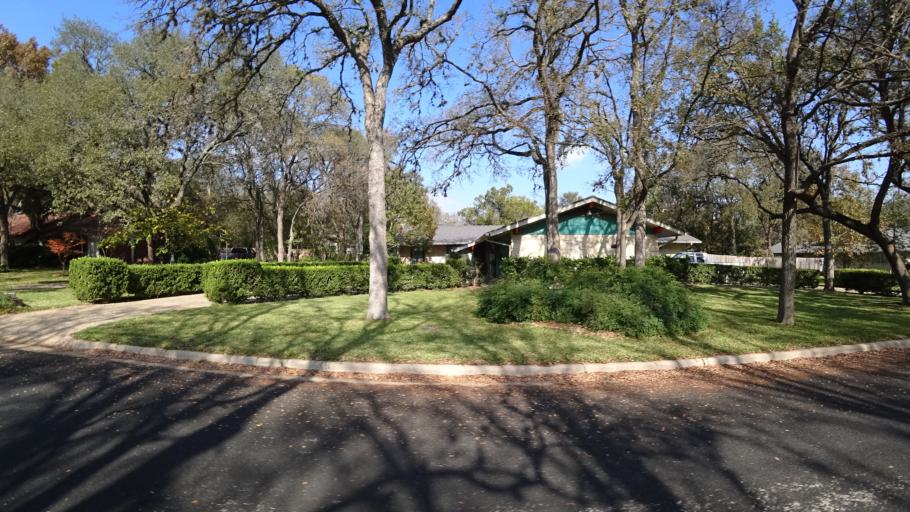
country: US
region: Texas
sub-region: Travis County
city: Shady Hollow
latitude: 30.1674
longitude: -97.8629
